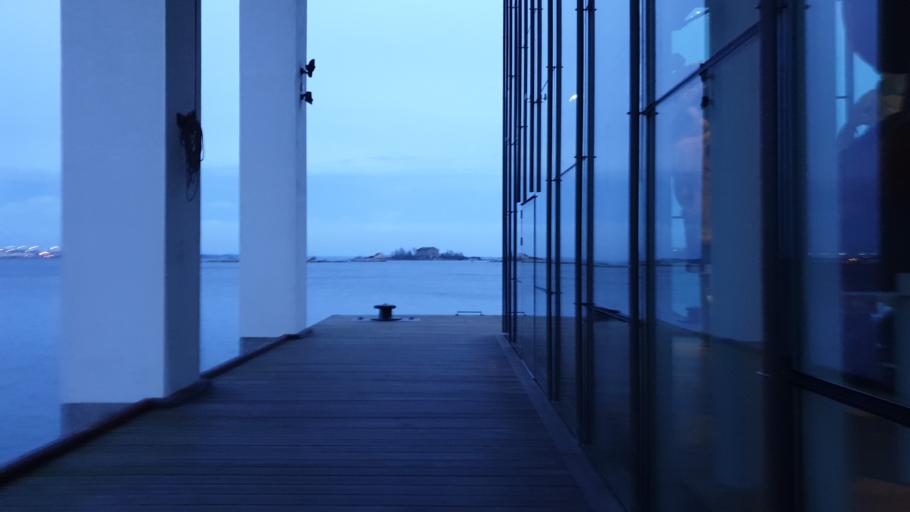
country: SE
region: Blekinge
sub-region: Karlskrona Kommun
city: Karlskrona
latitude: 56.1622
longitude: 15.5999
